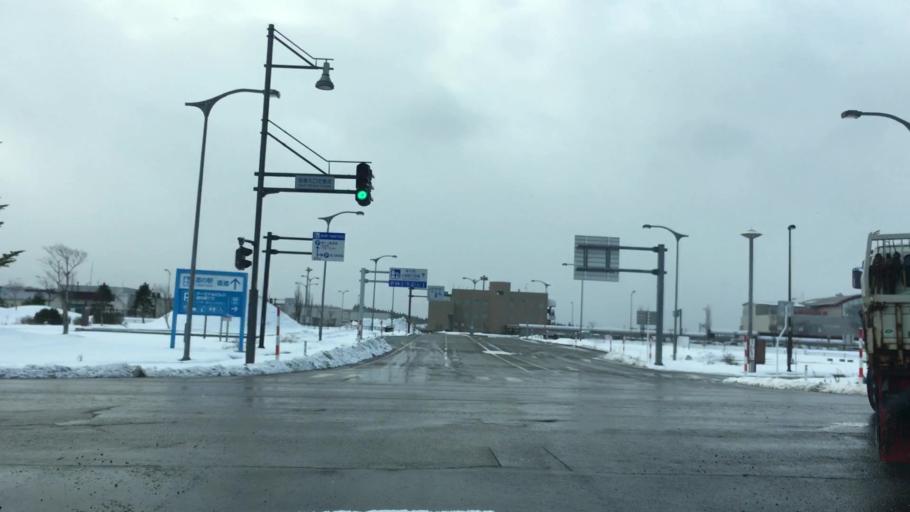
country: JP
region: Akita
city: Takanosu
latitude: 40.1978
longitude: 140.3742
